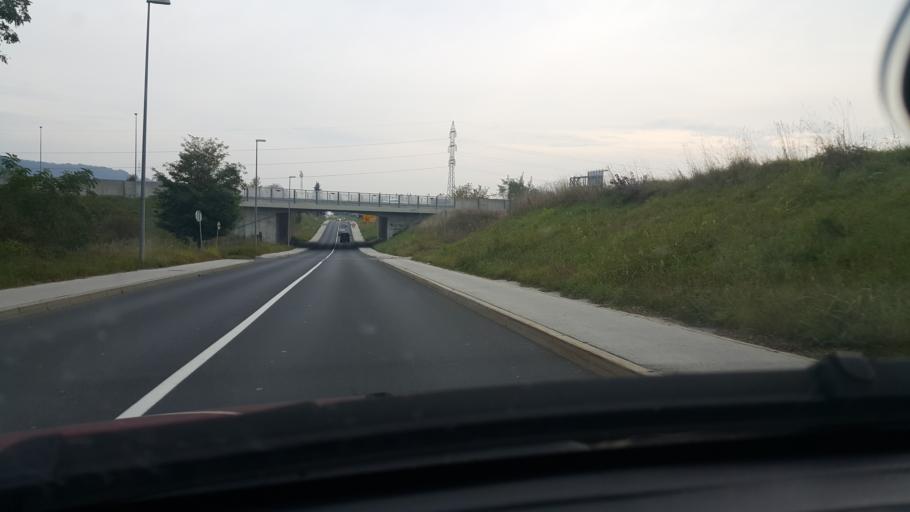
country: SI
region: Miklavz na Dravskem Polju
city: Miklavz na Dravskem Polju
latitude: 46.5290
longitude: 15.6972
